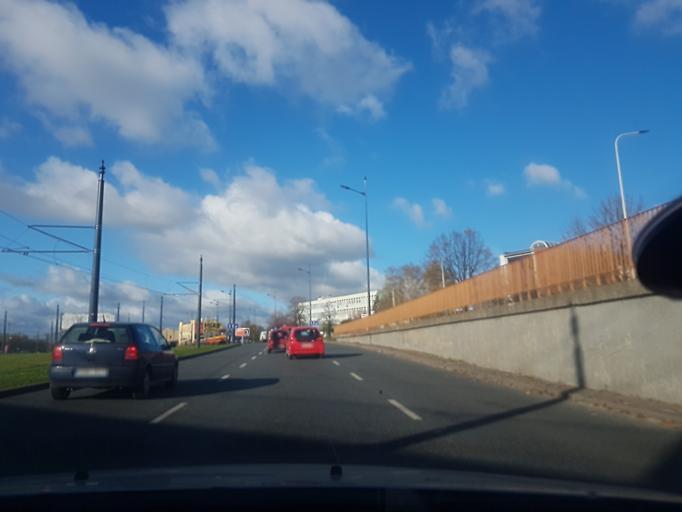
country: PL
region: Lodz Voivodeship
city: Lodz
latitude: 51.7640
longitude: 19.5199
